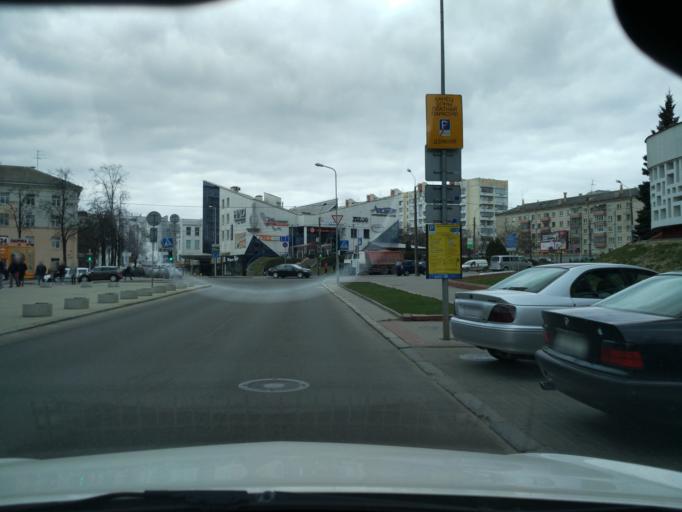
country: BY
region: Minsk
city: Minsk
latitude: 53.9249
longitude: 27.5939
